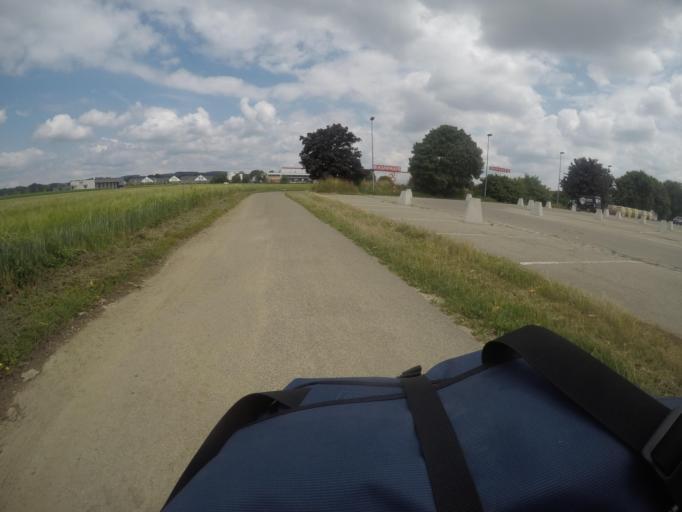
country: DE
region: Bavaria
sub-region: Swabia
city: Memmingen
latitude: 48.0051
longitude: 10.1687
